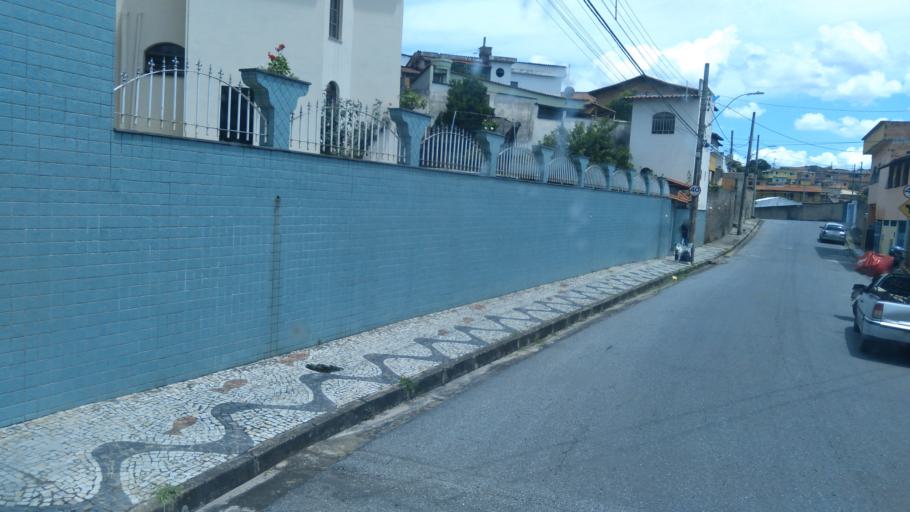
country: BR
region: Minas Gerais
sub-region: Belo Horizonte
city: Belo Horizonte
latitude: -19.8641
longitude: -43.8980
